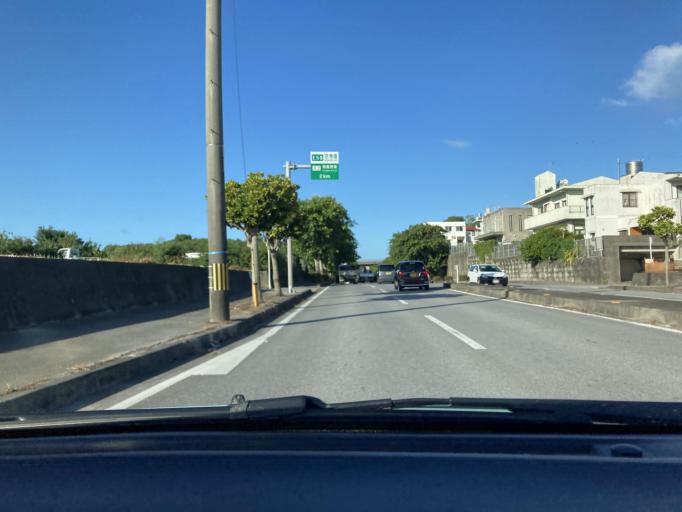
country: JP
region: Okinawa
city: Tomigusuku
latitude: 26.1733
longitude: 127.7113
